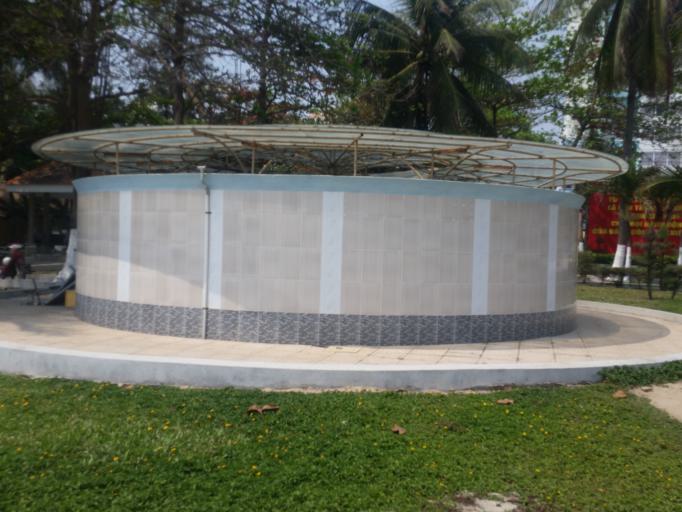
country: VN
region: Khanh Hoa
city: Nha Trang
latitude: 12.2319
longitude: 109.1988
